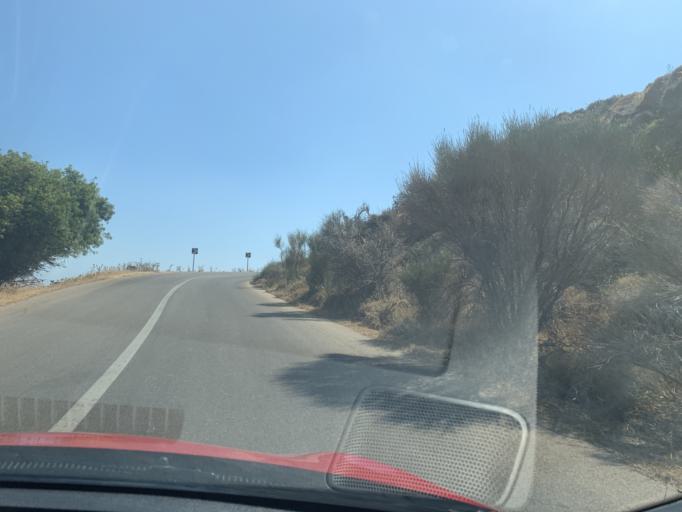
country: GR
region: North Aegean
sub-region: Chios
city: Vrontados
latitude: 38.4794
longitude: 25.8931
